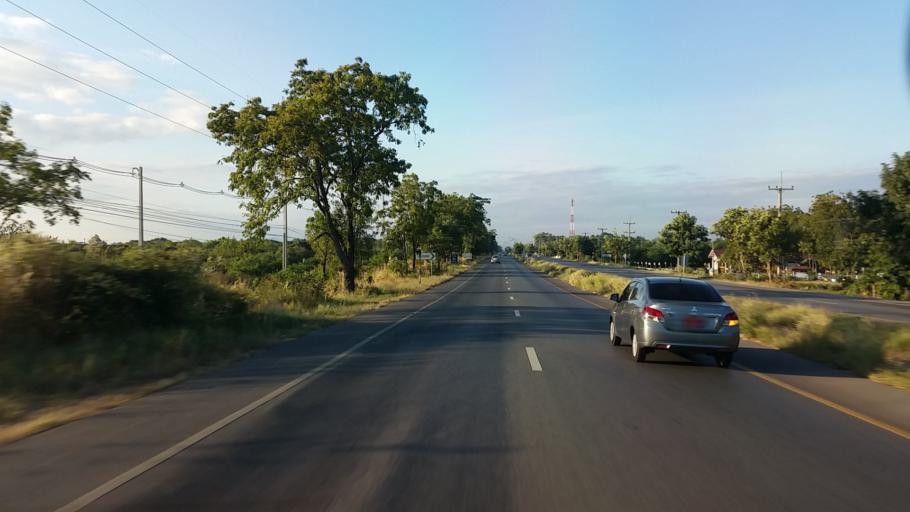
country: TH
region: Lop Buri
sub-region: Amphoe Tha Luang
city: Tha Luang
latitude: 15.1294
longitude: 101.0387
